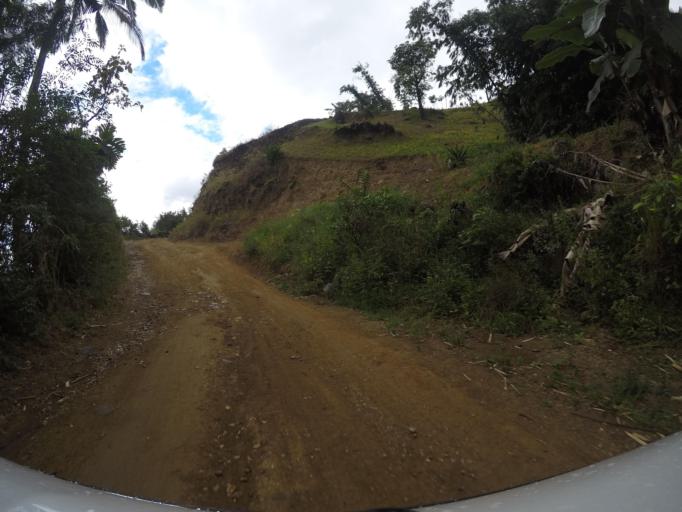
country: TL
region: Baucau
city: Baucau
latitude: -8.6426
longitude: 126.6359
